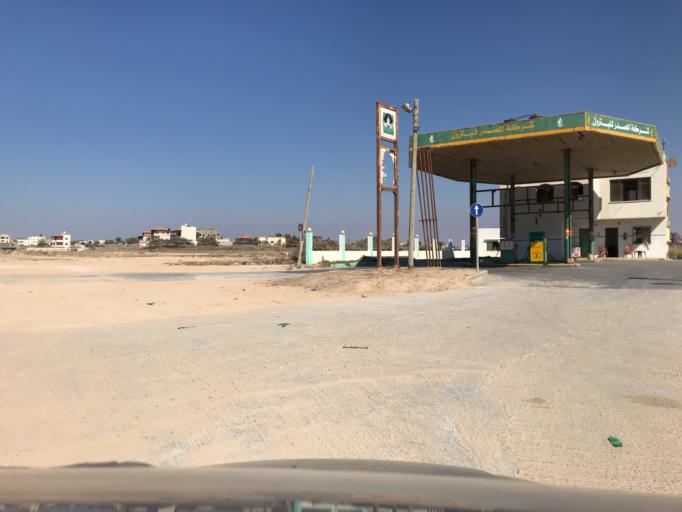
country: PS
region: Gaza Strip
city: Dayr al Balah
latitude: 31.4346
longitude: 34.3477
